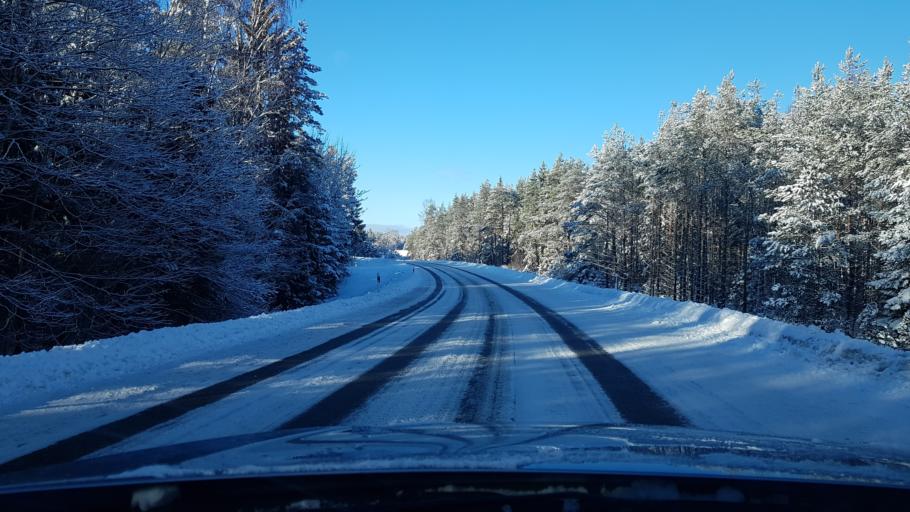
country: EE
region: Hiiumaa
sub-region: Kaerdla linn
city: Kardla
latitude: 58.9722
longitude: 22.7674
